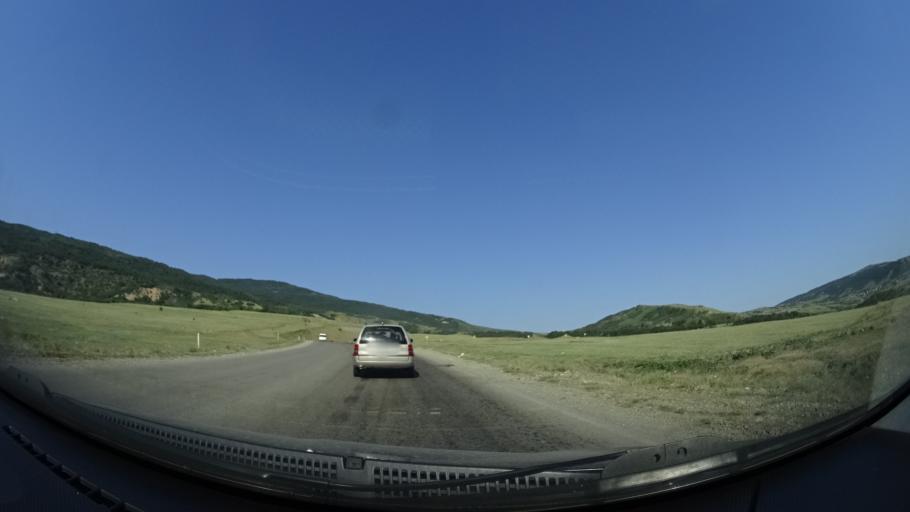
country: GE
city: Didi Lilo
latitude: 41.8011
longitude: 44.8875
